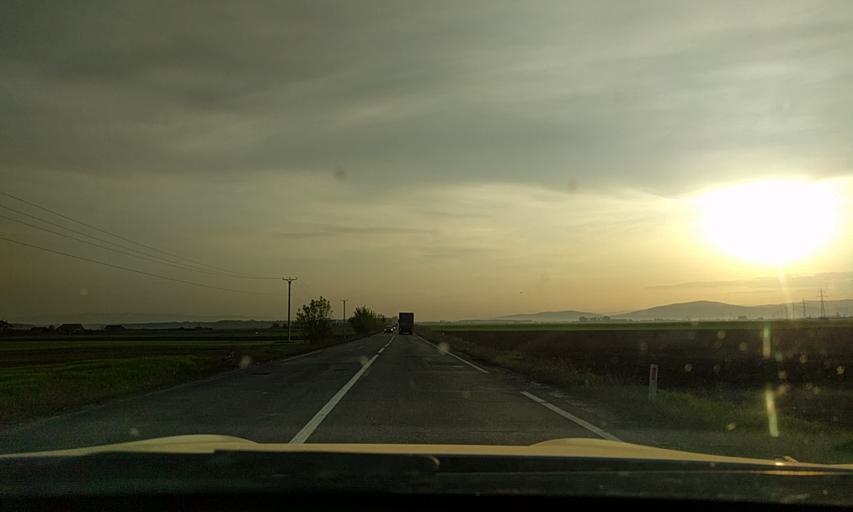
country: RO
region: Brasov
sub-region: Comuna Harman
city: Harman
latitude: 45.7153
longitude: 25.7138
